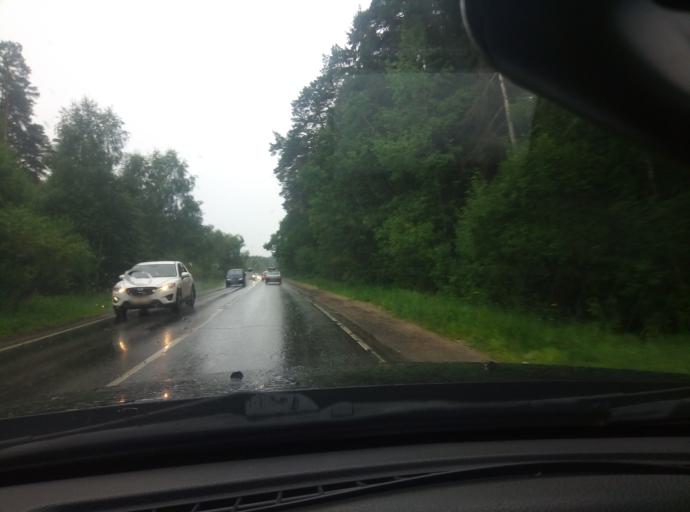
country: RU
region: Moskovskaya
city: Protvino
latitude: 54.8862
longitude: 37.1739
